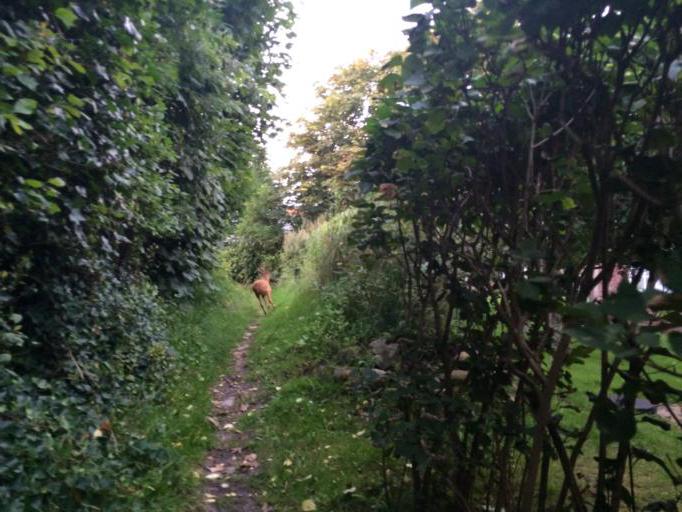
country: DK
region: South Denmark
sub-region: Fano Kommune
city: Nordby
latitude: 55.3488
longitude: 8.4715
